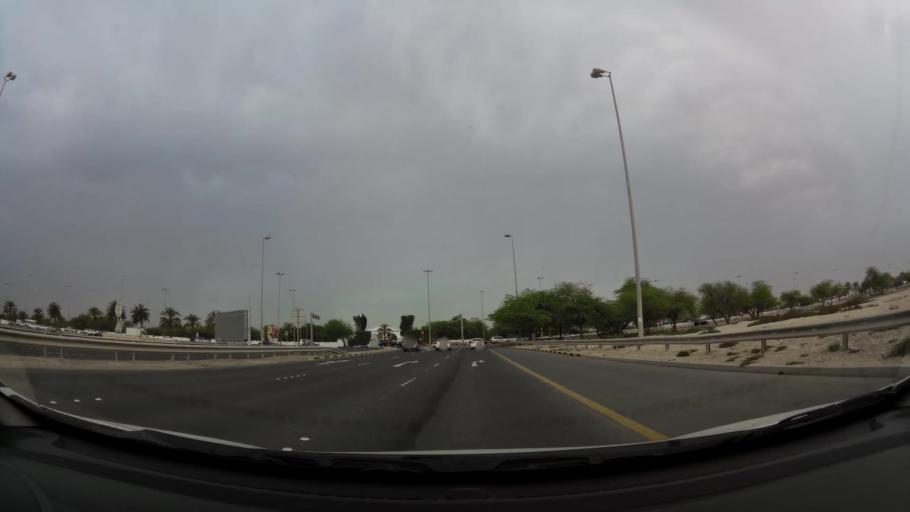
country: BH
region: Central Governorate
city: Dar Kulayb
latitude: 26.0560
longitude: 50.4999
